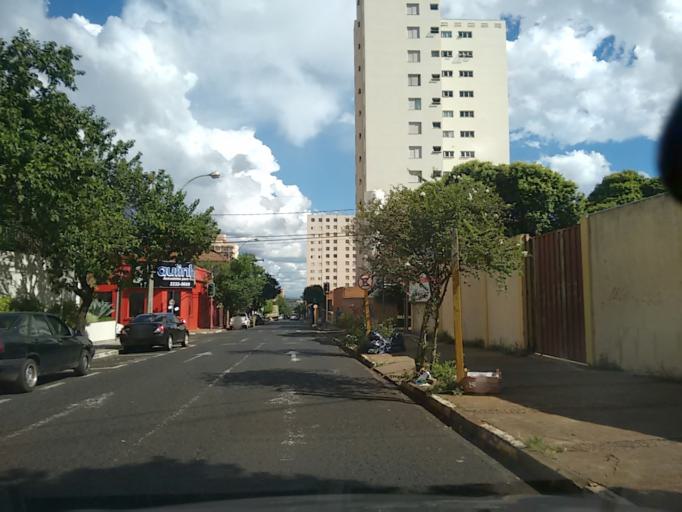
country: BR
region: Sao Paulo
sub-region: Araraquara
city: Araraquara
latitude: -21.7948
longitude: -48.1787
